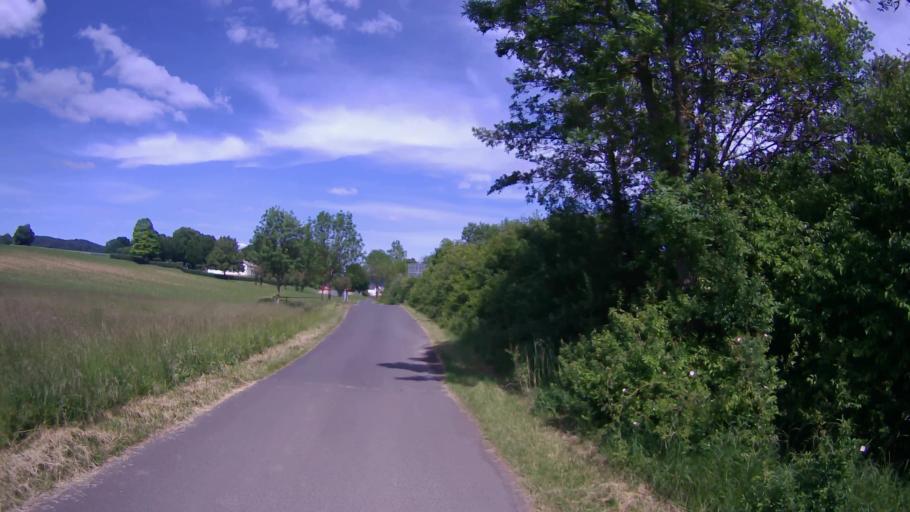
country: DE
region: Hesse
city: Hain-Grundau
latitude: 50.2373
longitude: 9.1277
